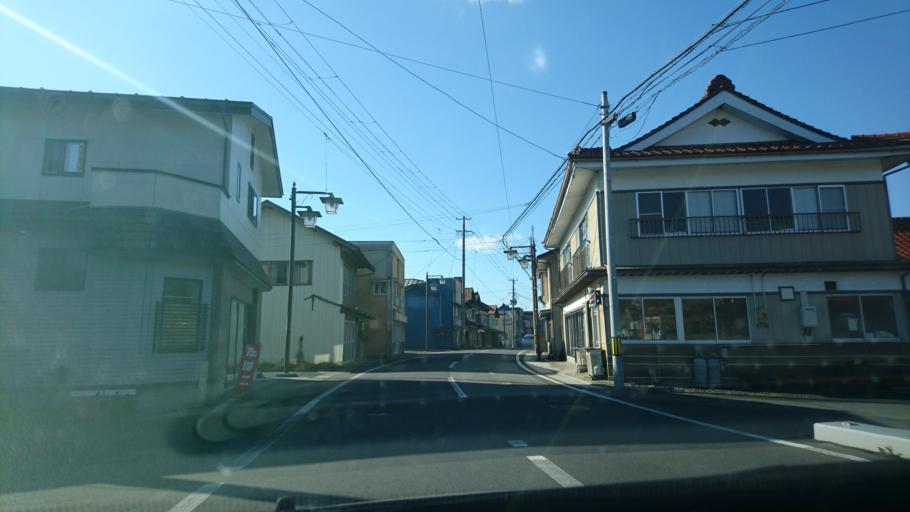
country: JP
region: Iwate
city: Ichinoseki
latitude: 39.0170
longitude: 141.4033
